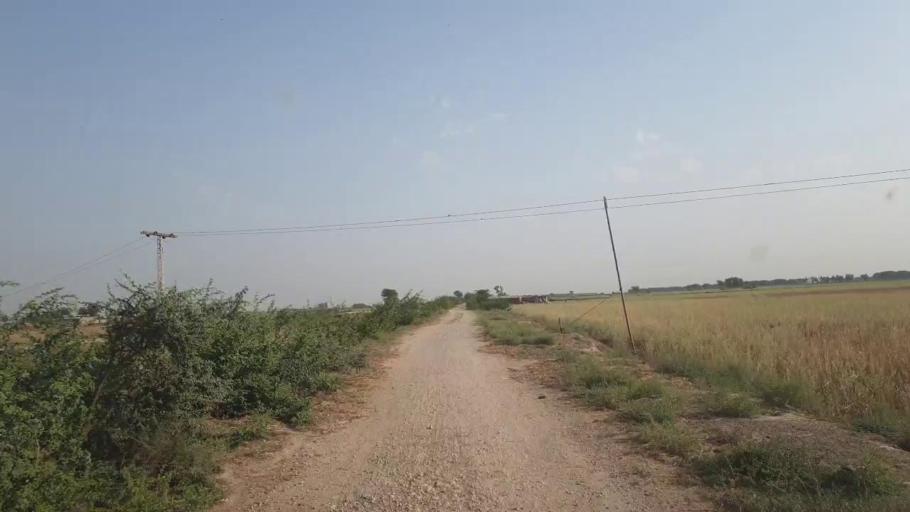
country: PK
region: Sindh
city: Kario
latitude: 24.5965
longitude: 68.5538
